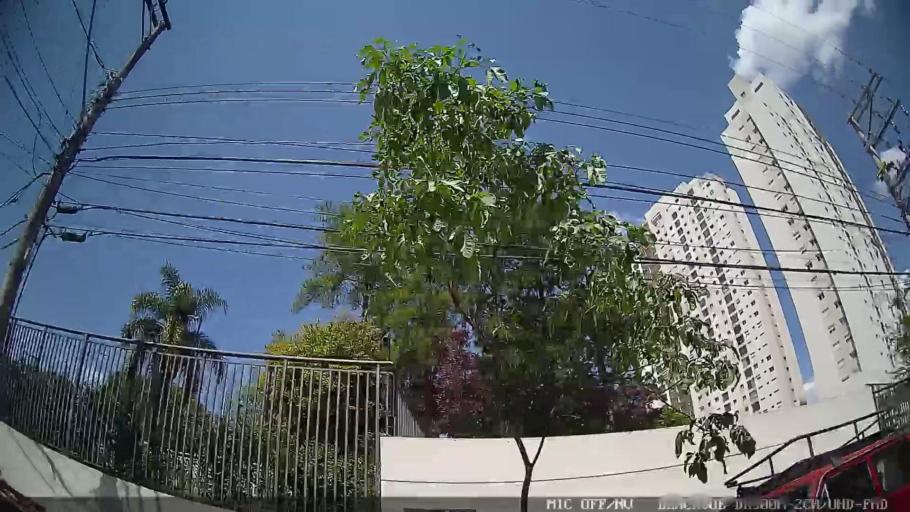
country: BR
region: Sao Paulo
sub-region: Guarulhos
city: Guarulhos
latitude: -23.5104
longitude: -46.5205
